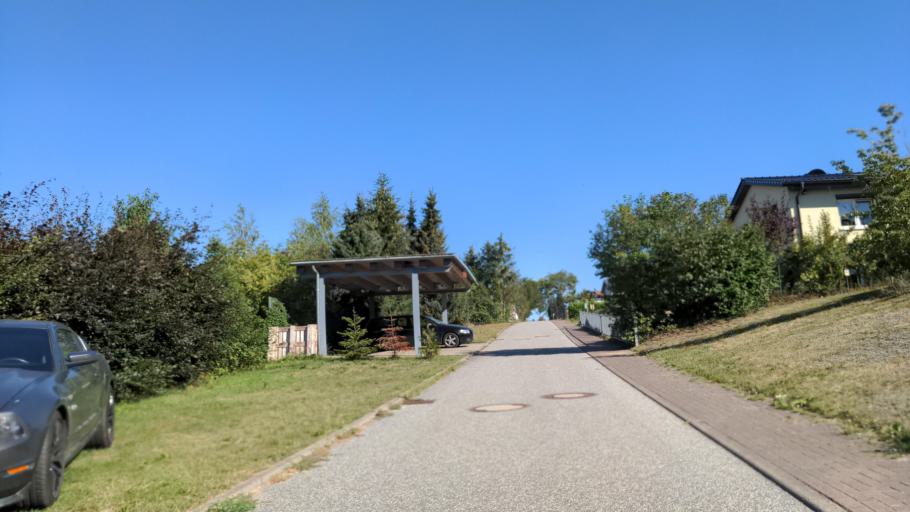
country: DE
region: Mecklenburg-Vorpommern
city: Gramkow
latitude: 53.9349
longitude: 11.3315
